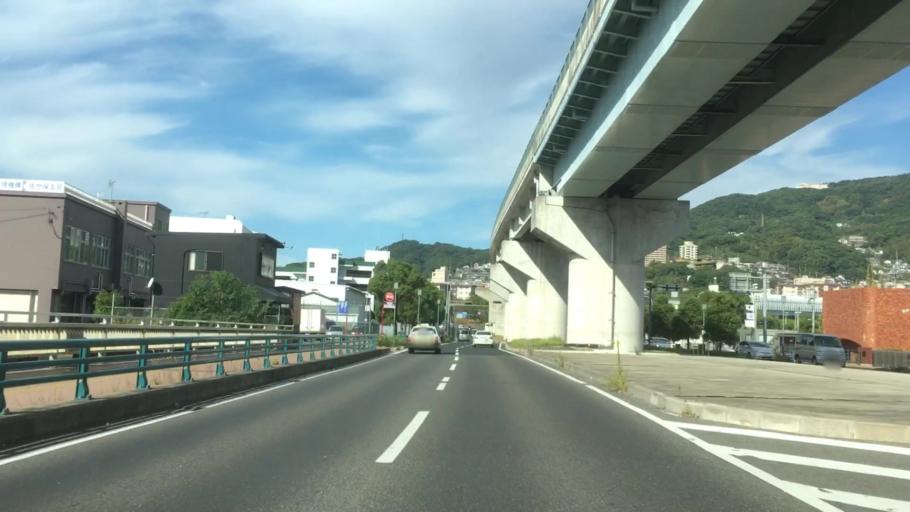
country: JP
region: Nagasaki
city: Sasebo
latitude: 33.1683
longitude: 129.7186
